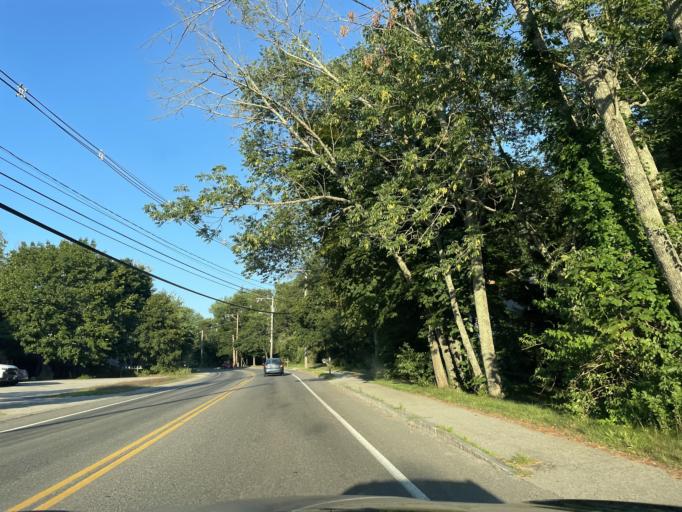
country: US
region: Massachusetts
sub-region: Plymouth County
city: Halifax
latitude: 41.9914
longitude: -70.8517
